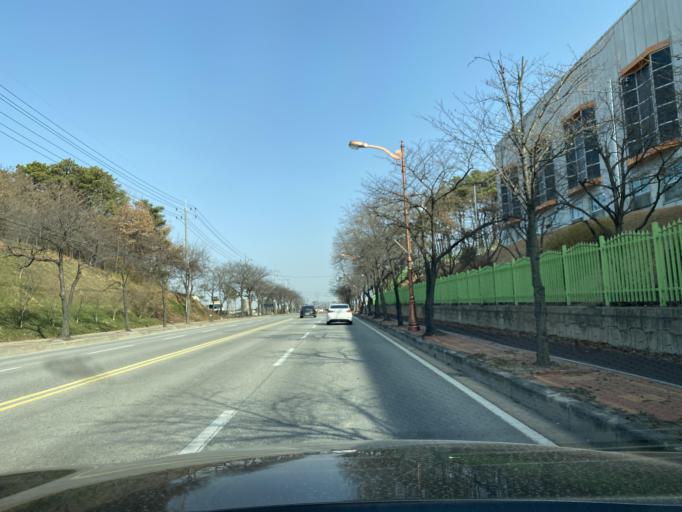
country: KR
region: Chungcheongnam-do
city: Yesan
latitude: 36.7157
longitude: 126.8432
